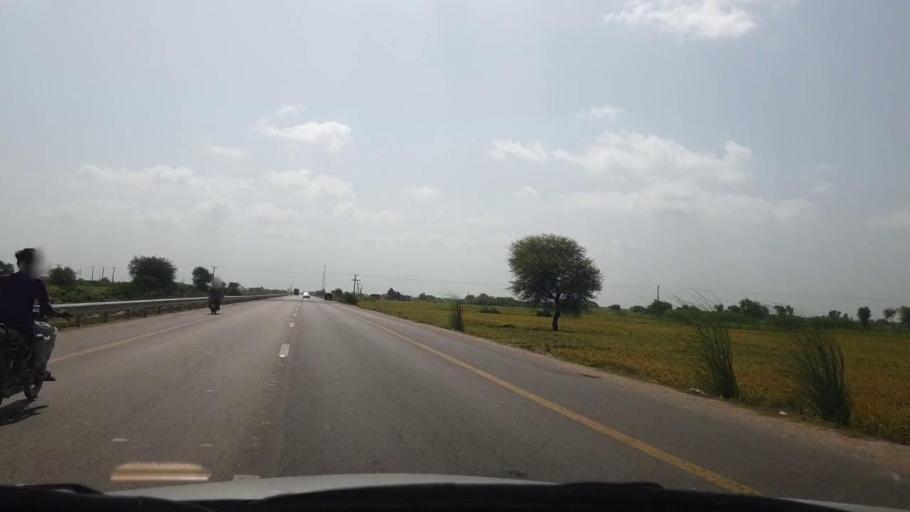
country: PK
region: Sindh
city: Matli
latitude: 24.9632
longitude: 68.6820
